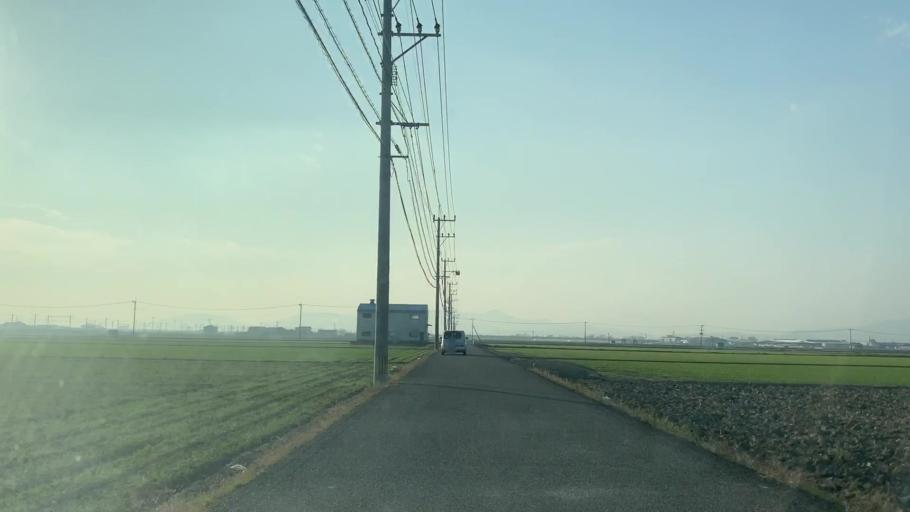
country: JP
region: Saga Prefecture
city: Saga-shi
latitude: 33.2607
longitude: 130.2601
